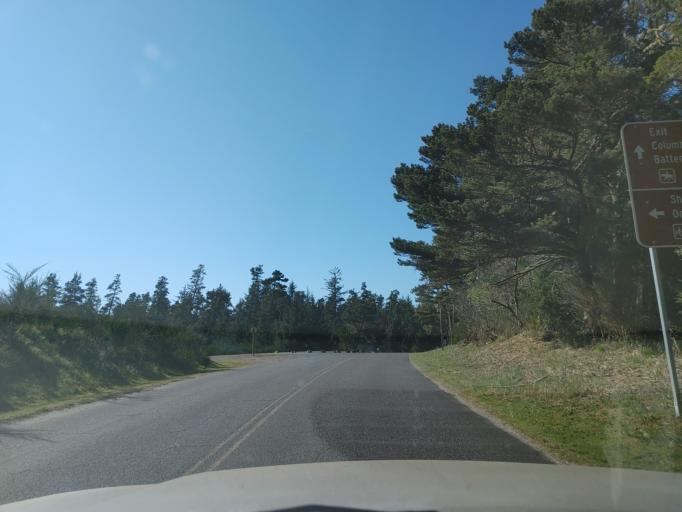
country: US
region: Oregon
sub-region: Clatsop County
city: Warrenton
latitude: 46.1798
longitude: -123.9697
